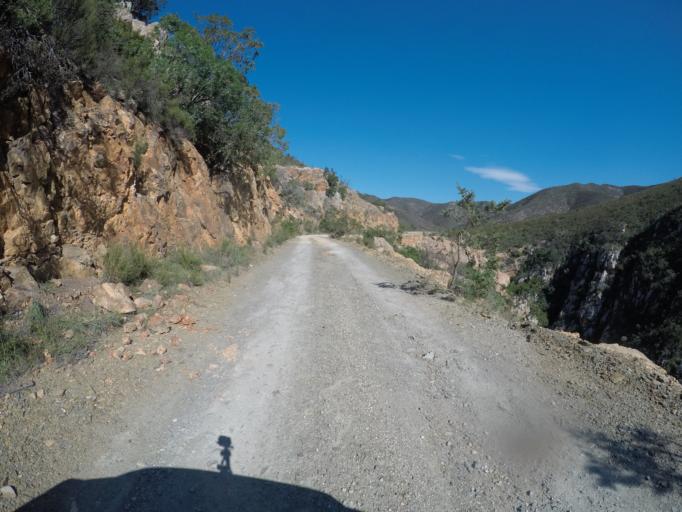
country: ZA
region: Eastern Cape
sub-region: Cacadu District Municipality
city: Kareedouw
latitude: -33.6522
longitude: 24.5038
